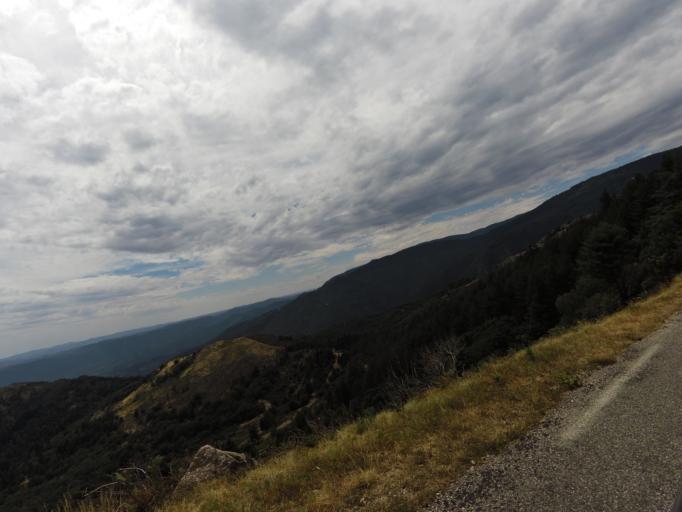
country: FR
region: Languedoc-Roussillon
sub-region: Departement du Gard
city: Valleraugue
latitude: 44.0423
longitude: 3.6091
